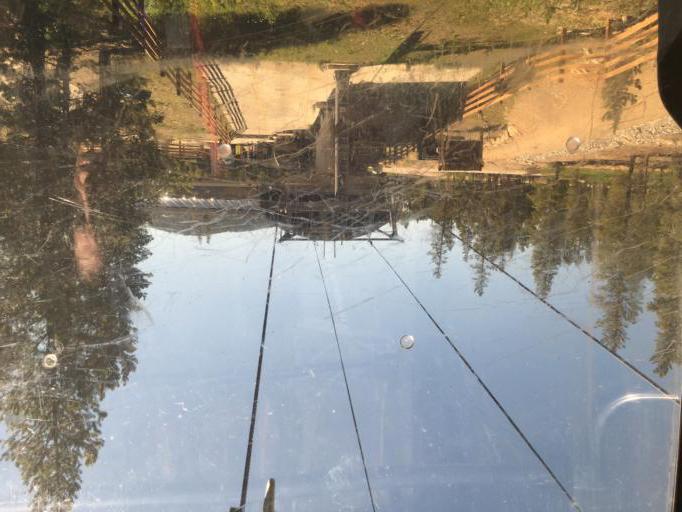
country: US
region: Colorado
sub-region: Summit County
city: Breckenridge
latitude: 39.4889
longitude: -106.0565
